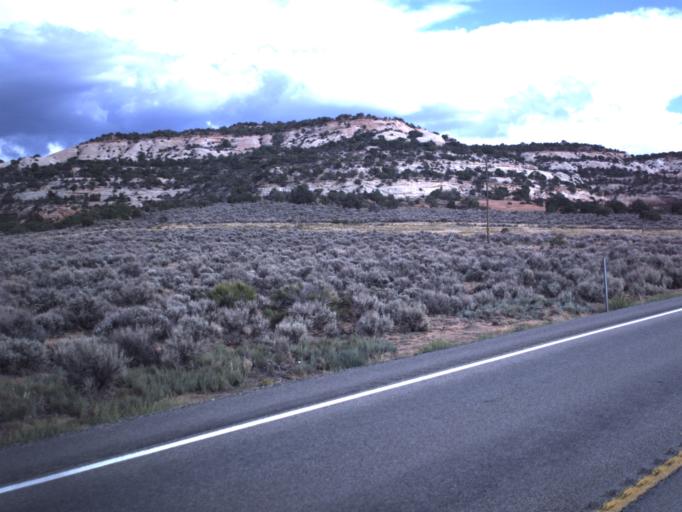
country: US
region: Utah
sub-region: Grand County
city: Moab
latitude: 38.2842
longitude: -109.3735
